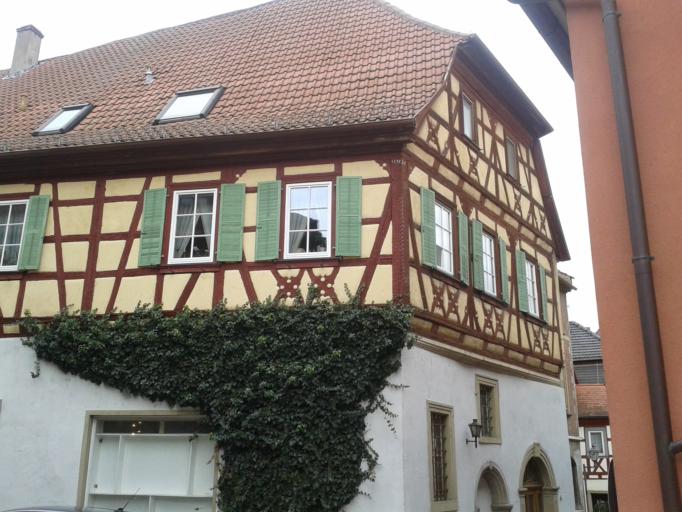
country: DE
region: Bavaria
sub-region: Regierungsbezirk Unterfranken
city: Marktbreit
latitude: 49.6664
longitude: 10.1433
